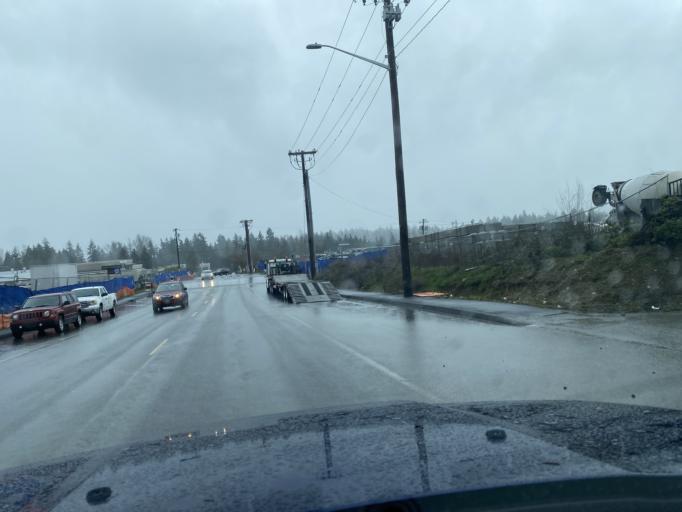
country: US
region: Washington
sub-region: King County
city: Bellevue
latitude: 47.6253
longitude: -122.1672
